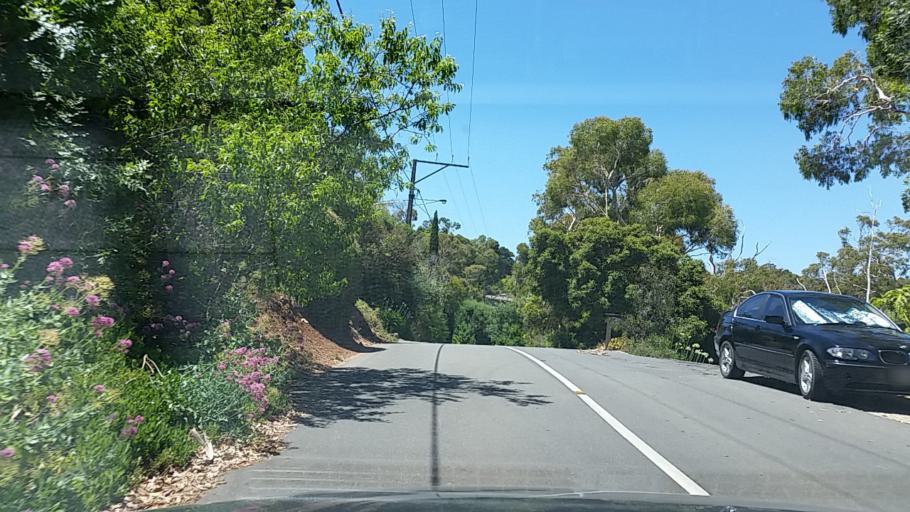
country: AU
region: South Australia
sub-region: Burnside
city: Mount Osmond
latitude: -34.9666
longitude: 138.6591
